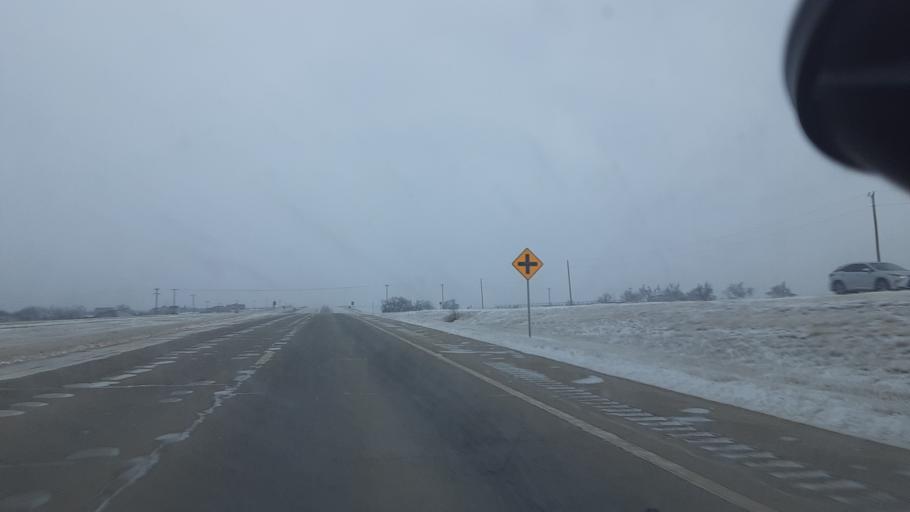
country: US
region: Oklahoma
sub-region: Logan County
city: Langston
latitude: 35.9295
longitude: -97.3178
